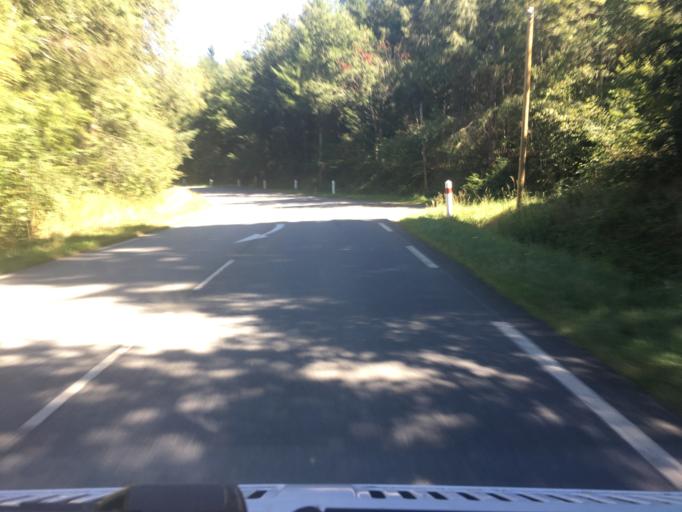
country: FR
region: Limousin
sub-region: Departement de la Correze
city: Bort-les-Orgues
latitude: 45.4126
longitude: 2.4679
